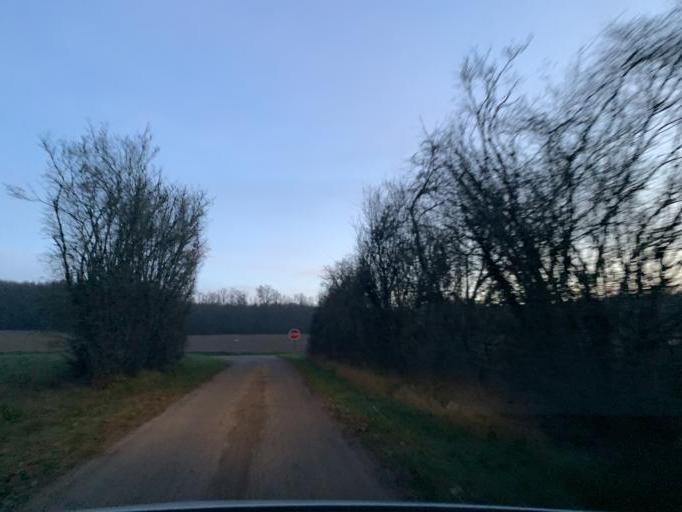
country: FR
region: Bourgogne
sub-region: Departement de l'Yonne
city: Fontenailles
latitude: 47.5548
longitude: 3.3660
